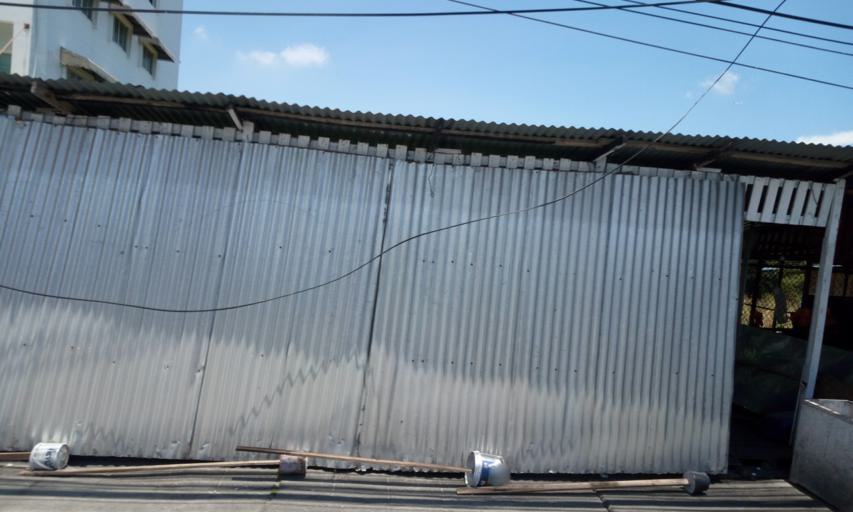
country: TH
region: Bangkok
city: Bang Na
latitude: 13.6304
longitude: 100.7080
